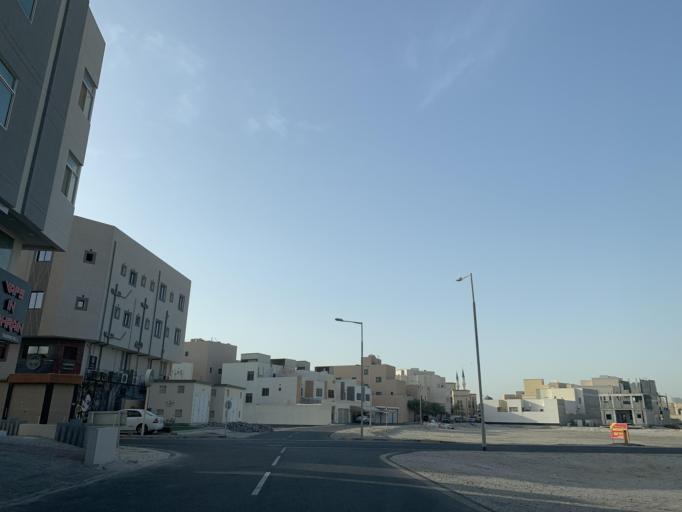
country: BH
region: Muharraq
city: Al Muharraq
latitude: 26.2810
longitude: 50.5979
